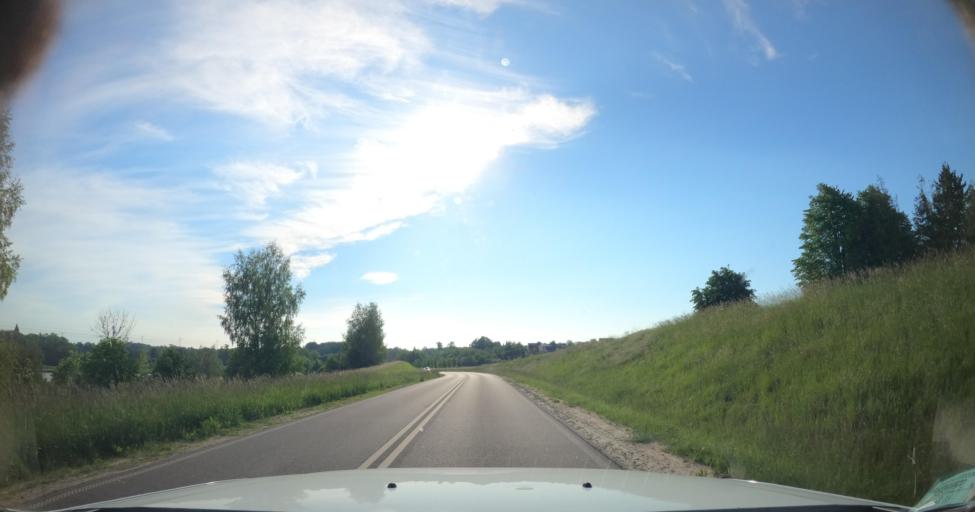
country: PL
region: Warmian-Masurian Voivodeship
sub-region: Powiat elblaski
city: Paslek
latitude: 54.0751
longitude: 19.6686
